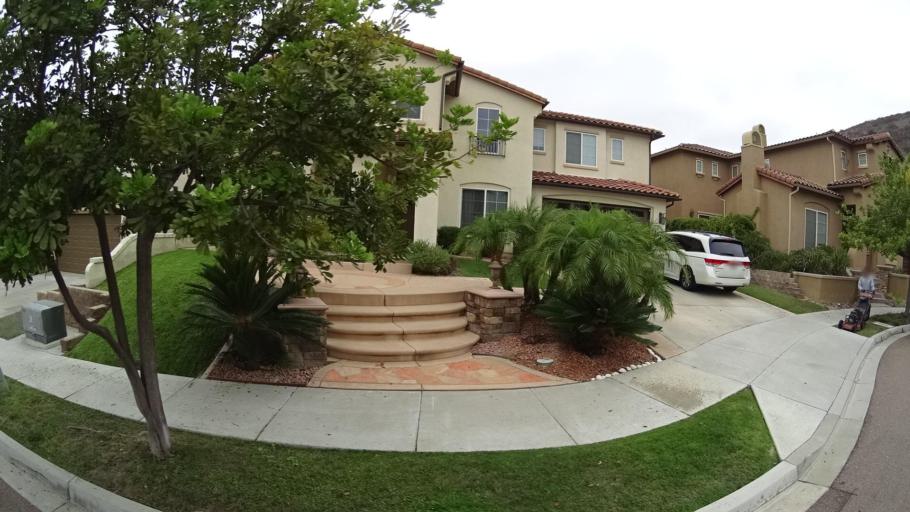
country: US
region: California
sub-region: San Diego County
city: Fairbanks Ranch
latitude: 33.0308
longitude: -117.1176
